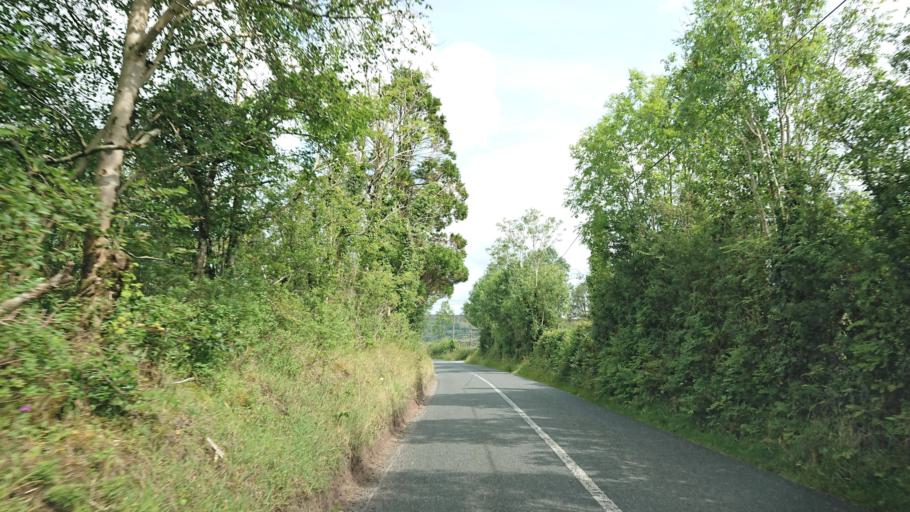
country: IE
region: Connaught
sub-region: County Leitrim
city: Carrick-on-Shannon
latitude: 54.0474
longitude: -8.1529
